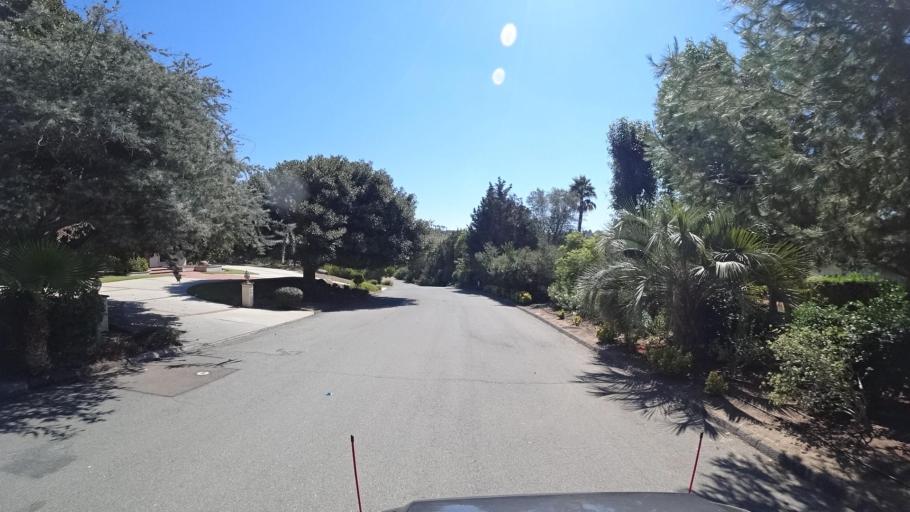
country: US
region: California
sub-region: San Diego County
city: Rancho Santa Fe
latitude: 33.0302
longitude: -117.1776
